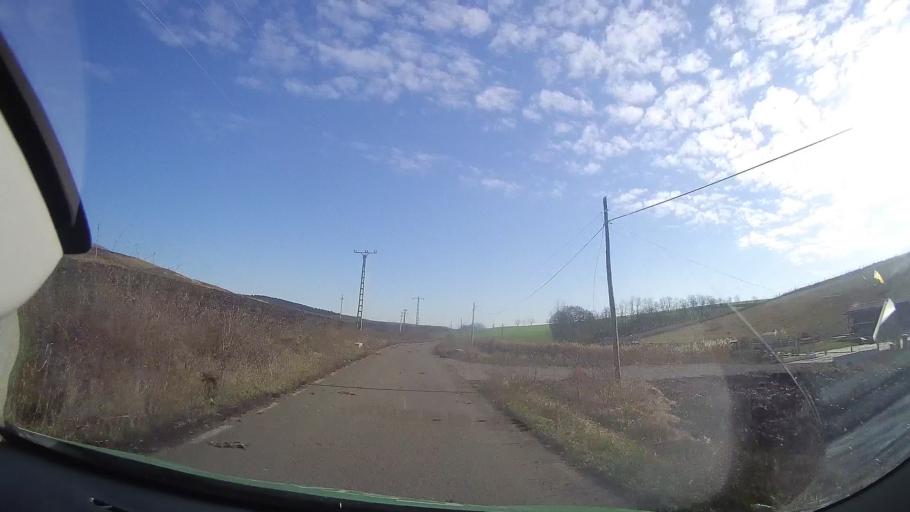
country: RO
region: Mures
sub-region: Comuna Saulia
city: Saulia
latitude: 46.6145
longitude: 24.2436
